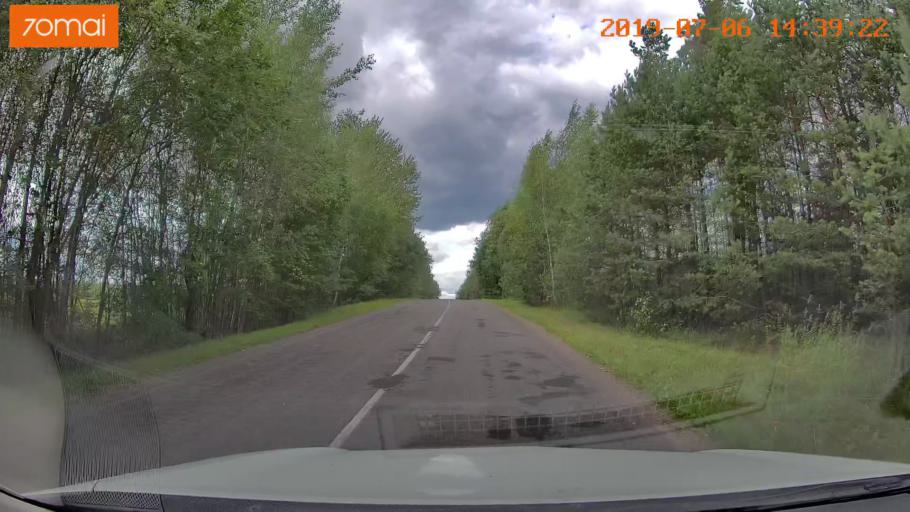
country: BY
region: Minsk
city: Ivyanyets
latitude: 53.9159
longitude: 26.6900
